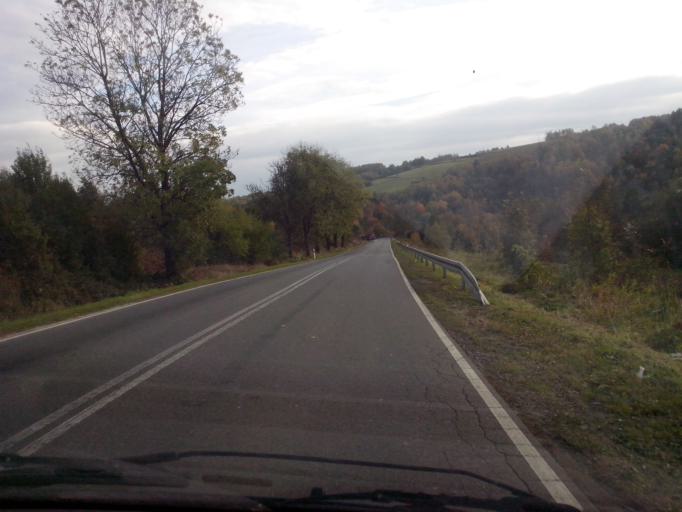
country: PL
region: Subcarpathian Voivodeship
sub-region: Powiat ropczycko-sedziszowski
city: Wielopole Skrzynskie
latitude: 49.9113
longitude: 21.6187
